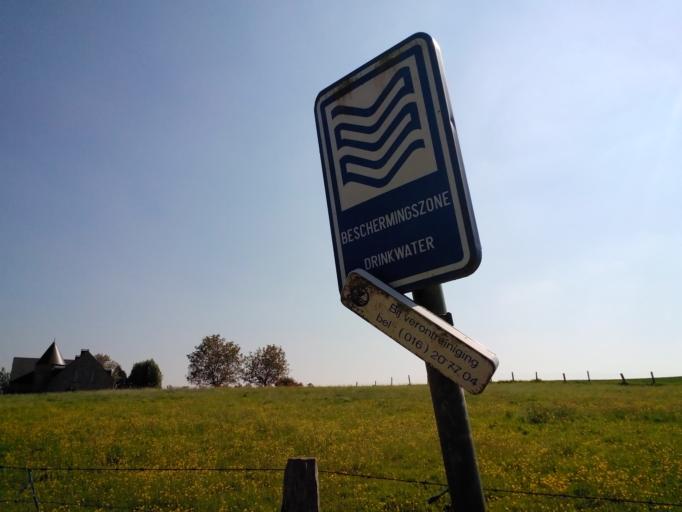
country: BE
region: Flanders
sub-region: Provincie Vlaams-Brabant
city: Bertem
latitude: 50.8691
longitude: 4.6264
